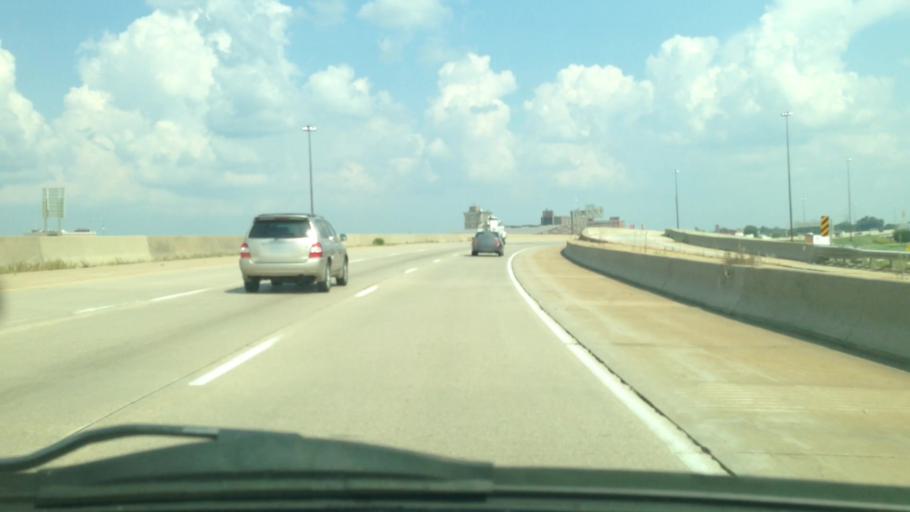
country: US
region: Iowa
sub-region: Black Hawk County
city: Waterloo
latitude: 42.4969
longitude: -92.3494
